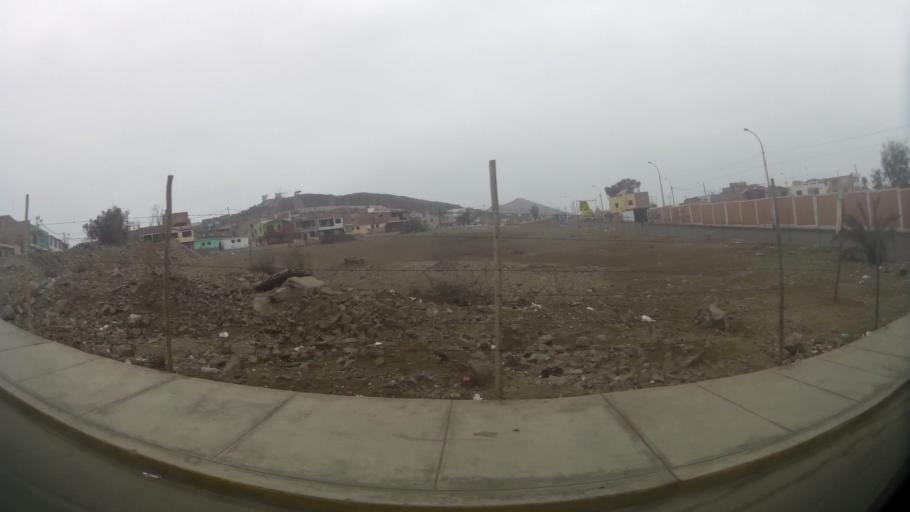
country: PE
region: Lima
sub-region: Provincia de Huaral
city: Chancay
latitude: -11.5872
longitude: -77.2706
